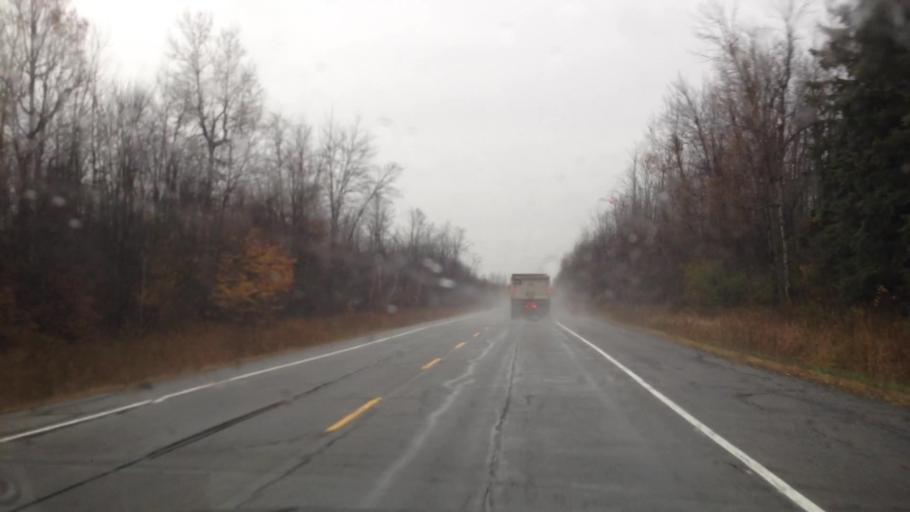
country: CA
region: Ontario
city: Clarence-Rockland
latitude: 45.3618
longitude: -75.3742
